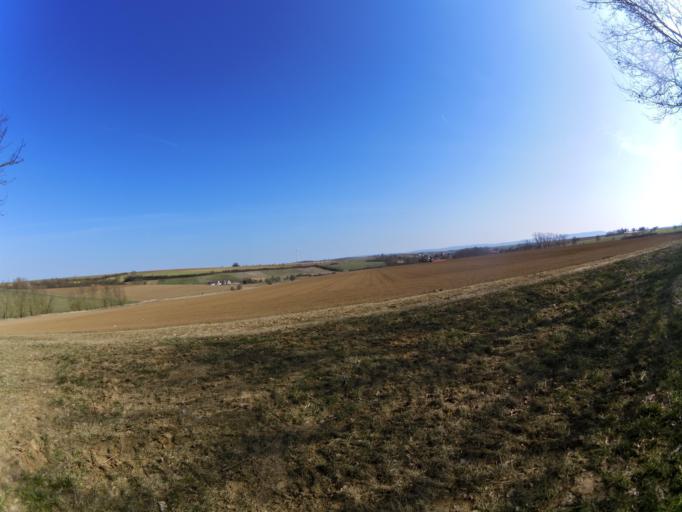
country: DE
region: Bavaria
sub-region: Regierungsbezirk Unterfranken
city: Prosselsheim
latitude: 49.8275
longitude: 10.1121
